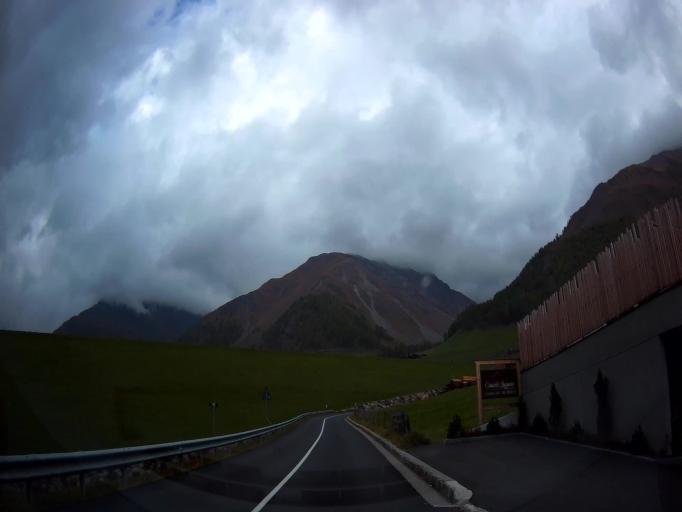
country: IT
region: Trentino-Alto Adige
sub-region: Bolzano
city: Senales
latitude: 46.7327
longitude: 10.8506
